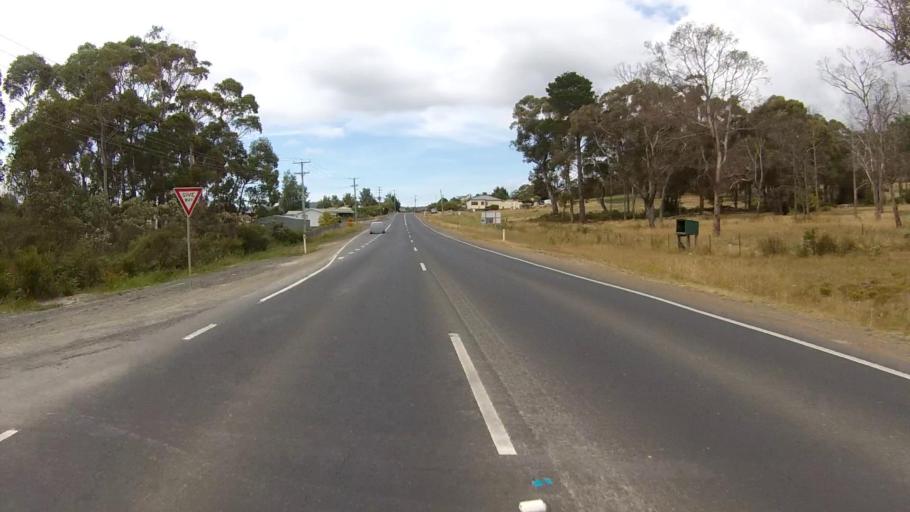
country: AU
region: Tasmania
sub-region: Kingborough
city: Margate
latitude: -43.0506
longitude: 147.2625
